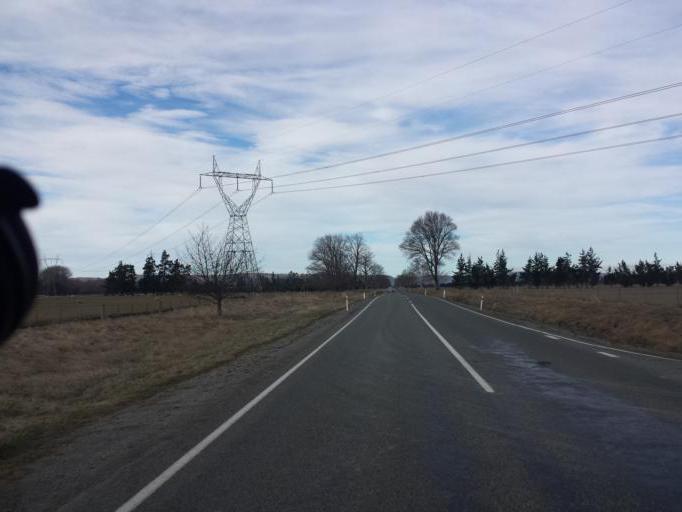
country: NZ
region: Canterbury
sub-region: Timaru District
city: Pleasant Point
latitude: -44.0595
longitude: 170.7763
